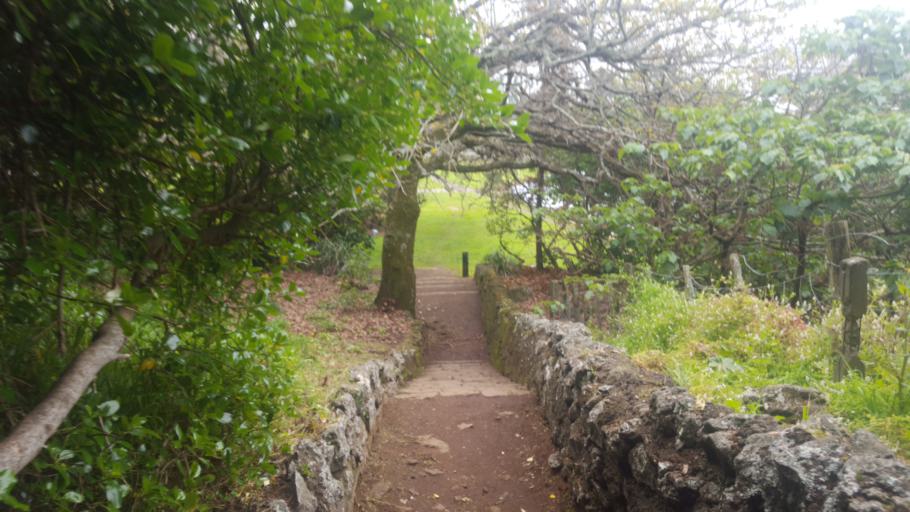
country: NZ
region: Auckland
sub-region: Auckland
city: Auckland
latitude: -36.8724
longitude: 174.7639
